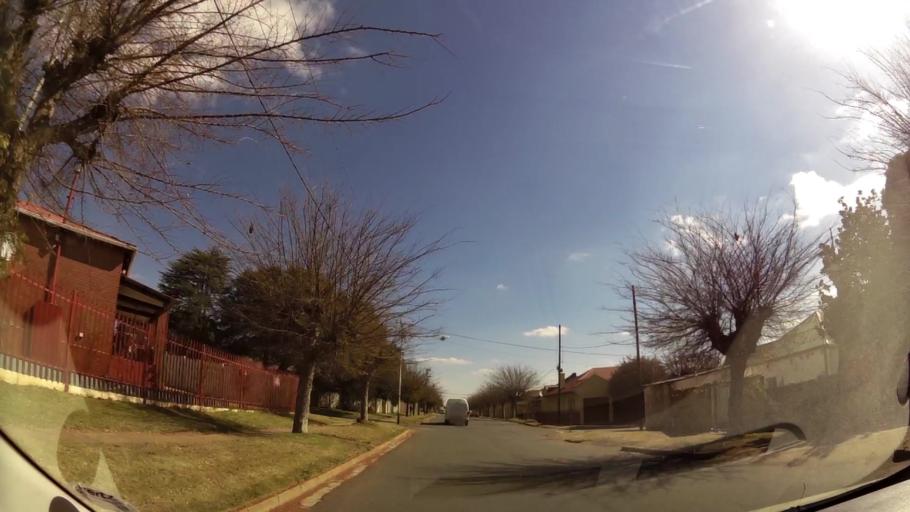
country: ZA
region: Gauteng
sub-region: West Rand District Municipality
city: Krugersdorp
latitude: -26.1090
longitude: 27.7839
